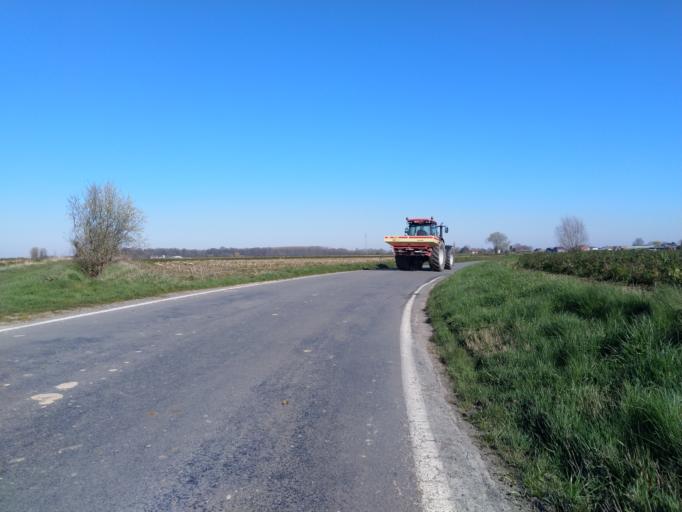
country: BE
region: Wallonia
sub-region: Province du Hainaut
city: Lens
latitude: 50.5371
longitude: 3.8584
